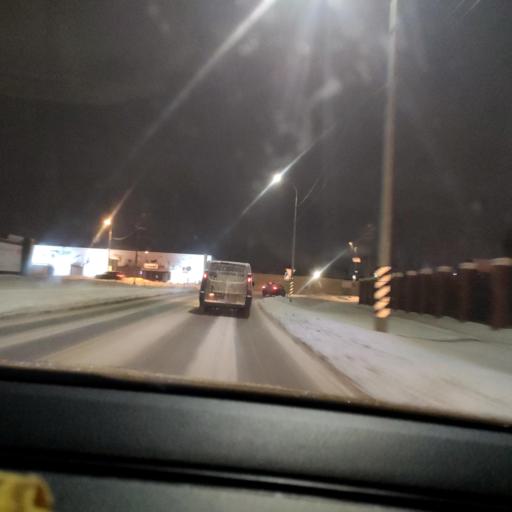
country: RU
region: Moskovskaya
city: Rozhdestveno
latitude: 55.8086
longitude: 36.9749
